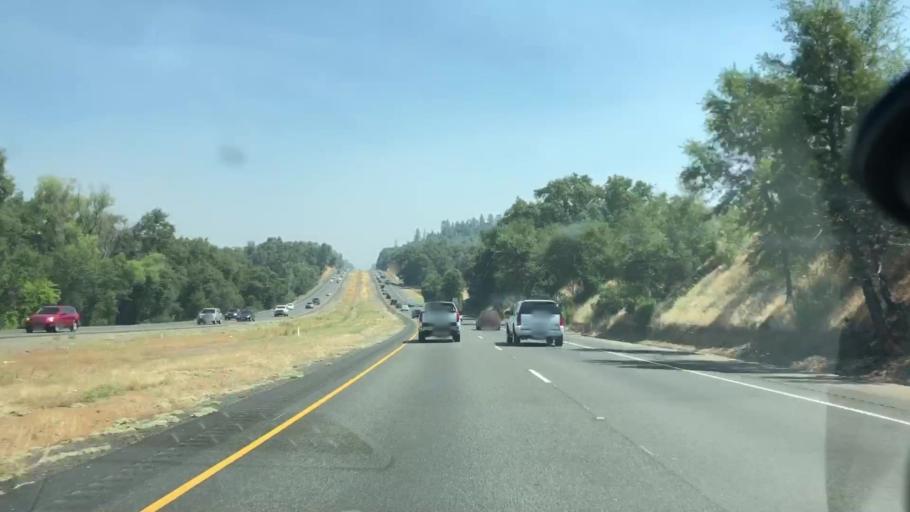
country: US
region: California
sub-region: El Dorado County
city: Shingle Springs
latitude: 38.6675
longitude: -120.9280
